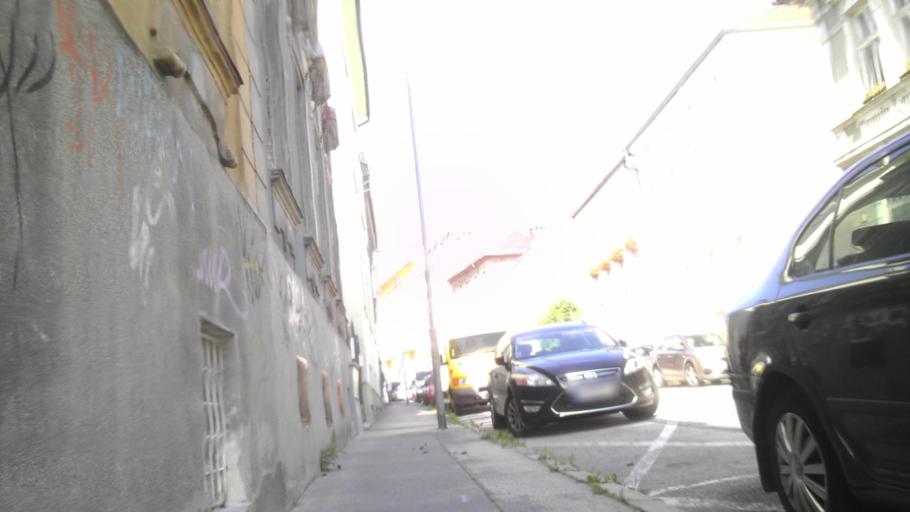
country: SK
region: Bratislavsky
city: Bratislava
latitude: 48.1541
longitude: 17.1092
